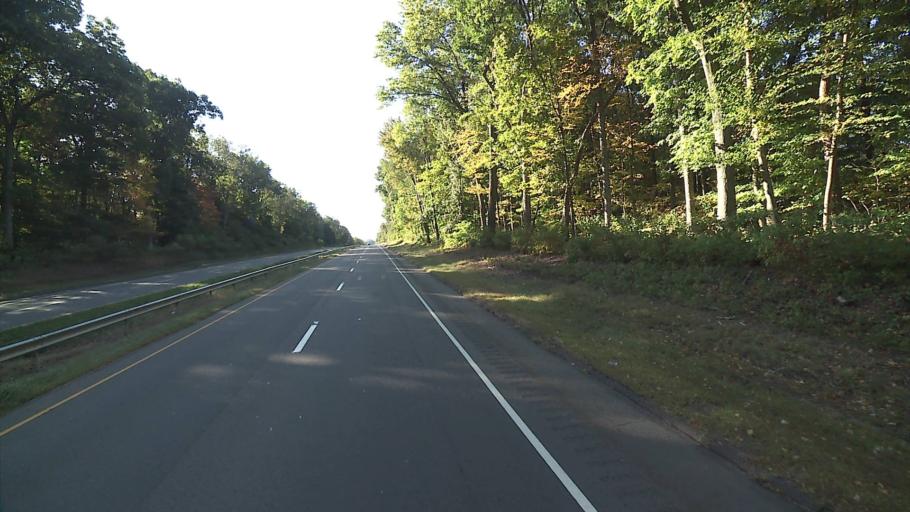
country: US
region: Connecticut
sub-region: New Haven County
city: Meriden
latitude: 41.5540
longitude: -72.7749
